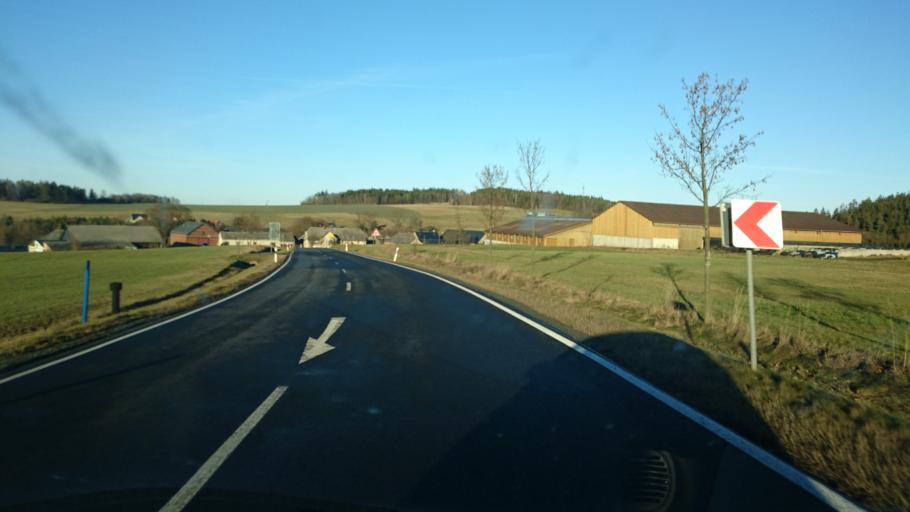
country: DE
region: Thuringia
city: Kirschkau
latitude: 50.6134
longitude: 11.9179
